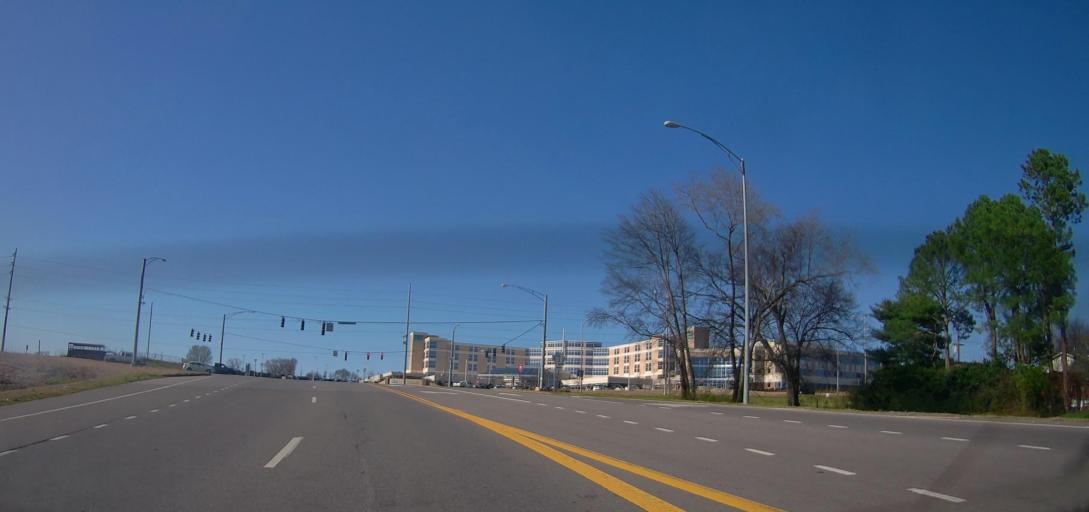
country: US
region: Alabama
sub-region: Lauderdale County
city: East Florence
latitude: 34.8028
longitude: -87.6512
